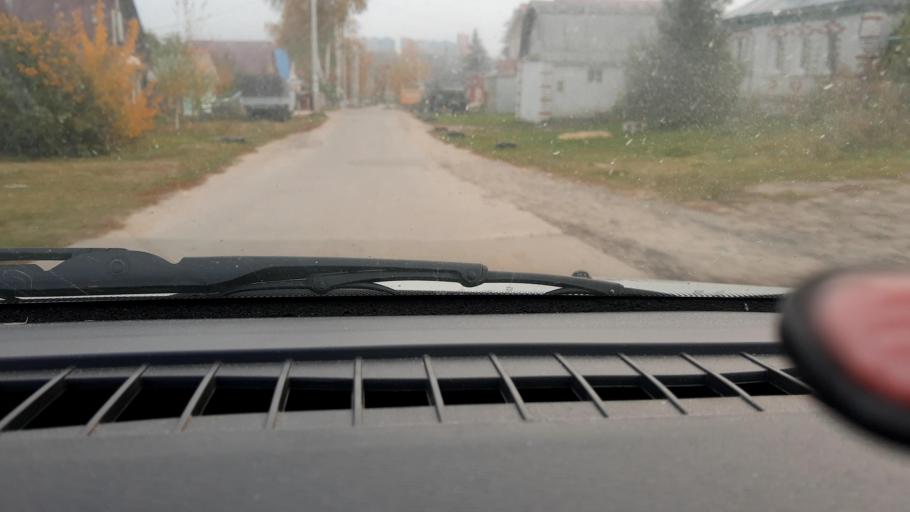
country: RU
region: Nizjnij Novgorod
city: Afonino
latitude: 56.2675
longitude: 44.0552
